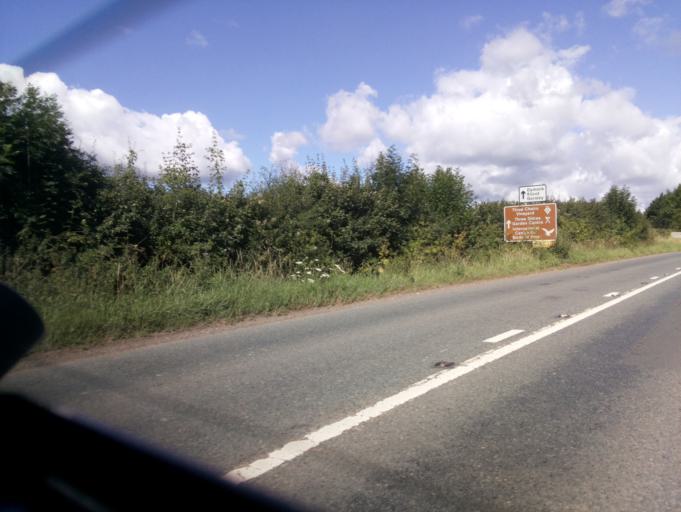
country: GB
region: England
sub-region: Gloucestershire
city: Newent
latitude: 51.9291
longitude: -2.3846
